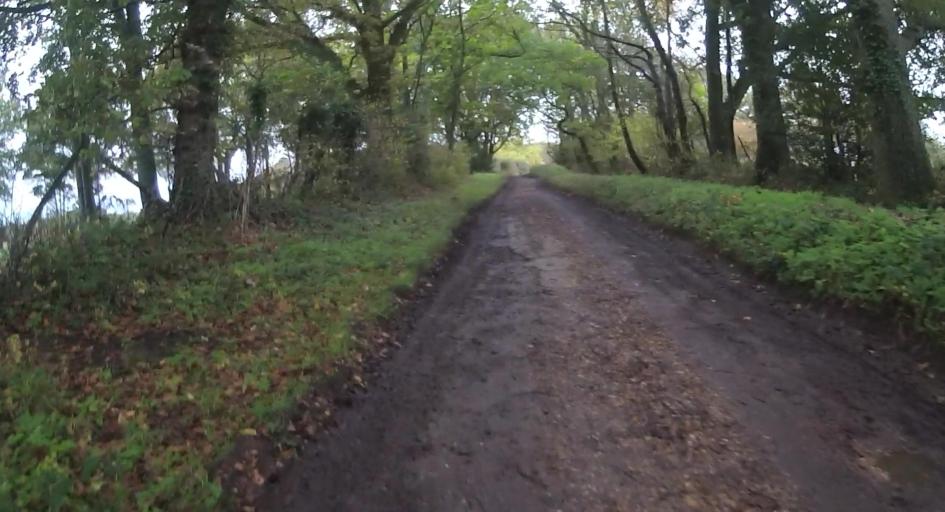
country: GB
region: England
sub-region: Surrey
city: Farnham
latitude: 51.2267
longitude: -0.8162
